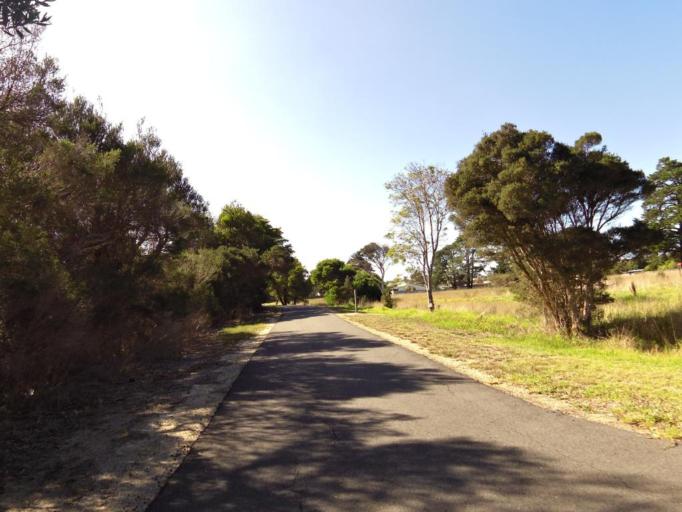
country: AU
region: Victoria
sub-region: Bass Coast
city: North Wonthaggi
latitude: -38.6049
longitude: 145.5814
